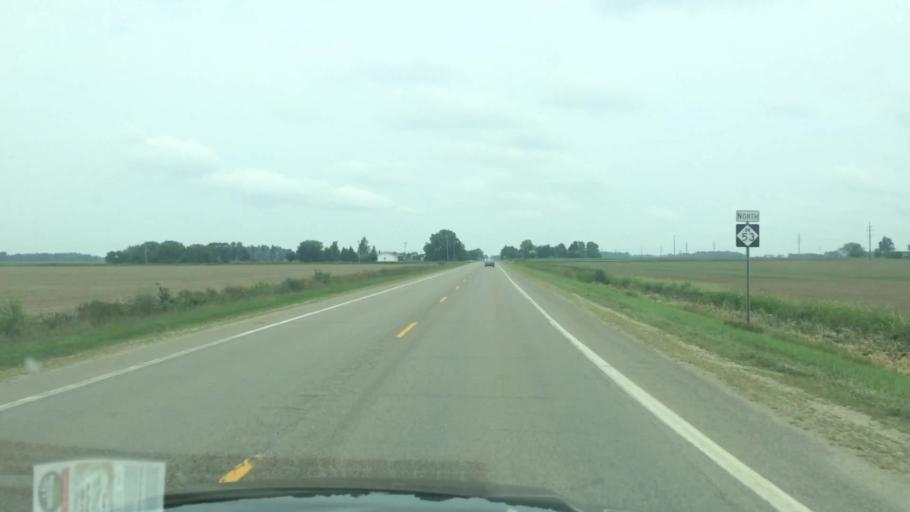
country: US
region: Michigan
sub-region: Huron County
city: Bad Axe
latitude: 43.8455
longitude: -83.0016
